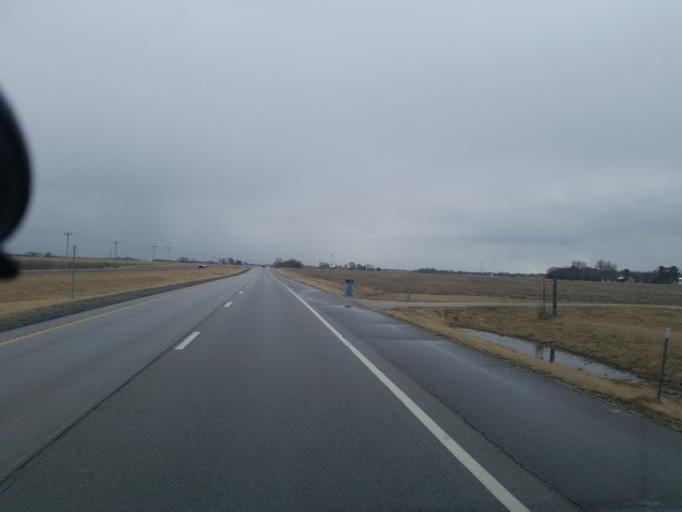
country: US
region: Missouri
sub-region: Macon County
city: Macon
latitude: 39.8419
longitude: -92.4806
